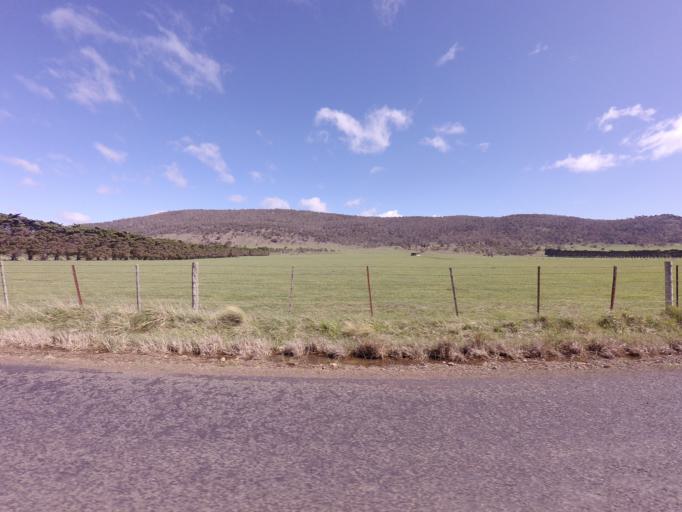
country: AU
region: Tasmania
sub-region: Northern Midlands
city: Evandale
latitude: -41.9654
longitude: 147.4406
